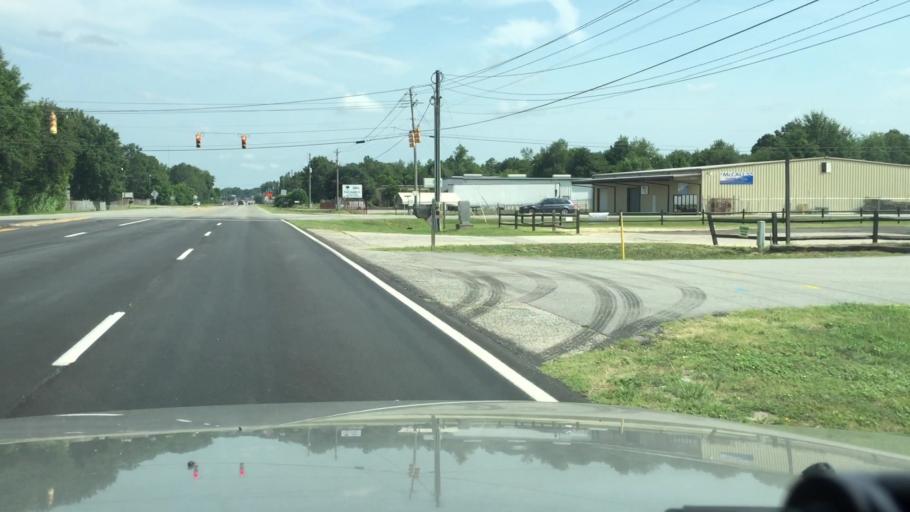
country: US
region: South Carolina
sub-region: Sumter County
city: South Sumter
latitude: 33.8883
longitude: -80.3507
